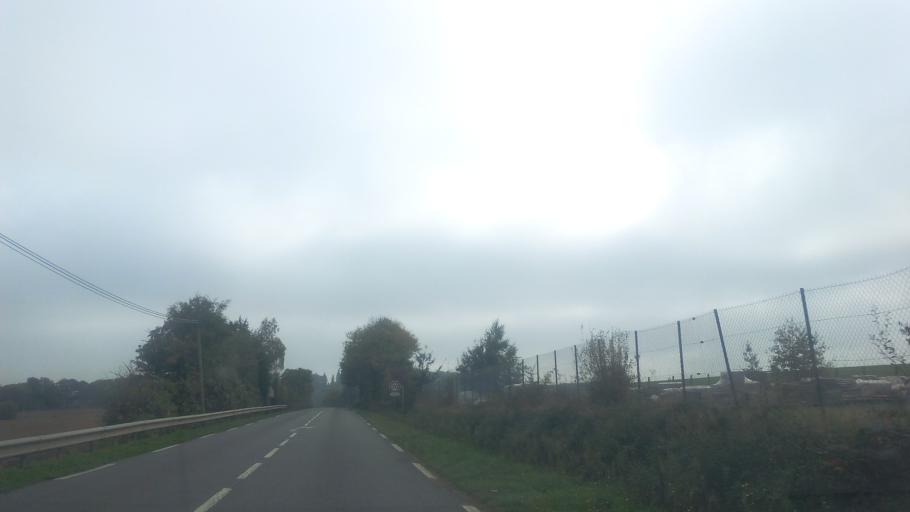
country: FR
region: Pays de la Loire
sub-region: Departement de la Loire-Atlantique
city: Guemene-Penfao
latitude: 47.6341
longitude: -1.9046
